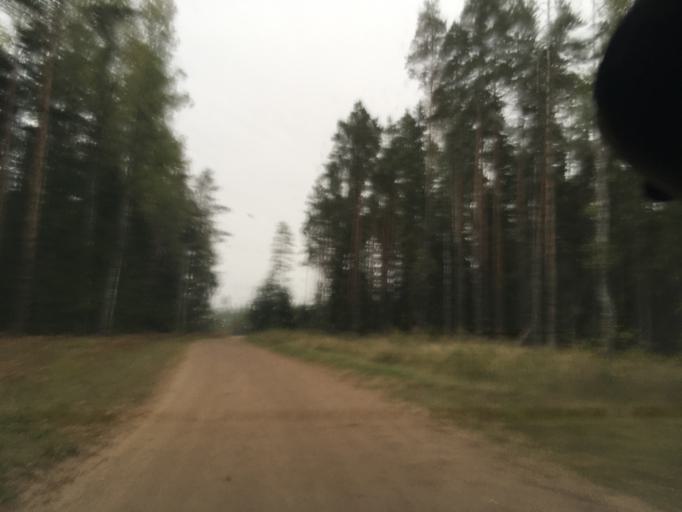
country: LV
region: Kuldigas Rajons
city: Kuldiga
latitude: 57.0186
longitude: 22.0023
